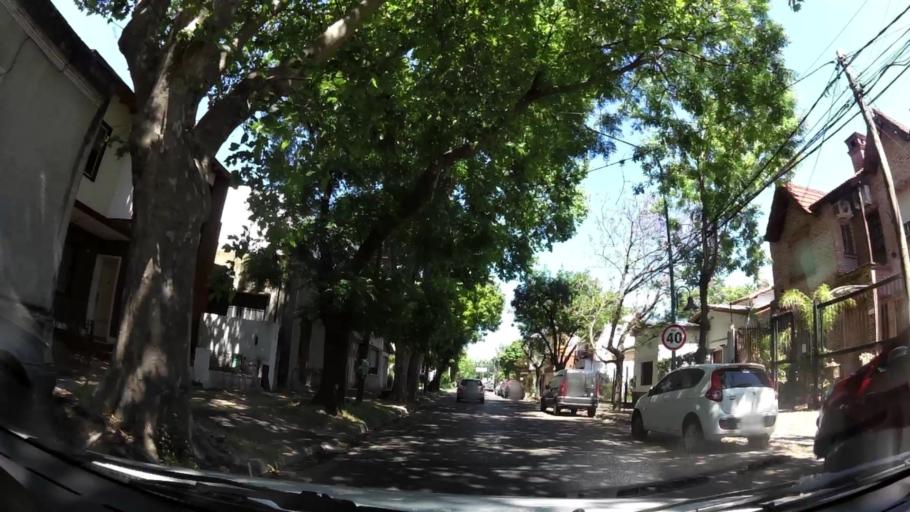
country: AR
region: Buenos Aires
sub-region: Partido de Vicente Lopez
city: Olivos
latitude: -34.5127
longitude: -58.5020
